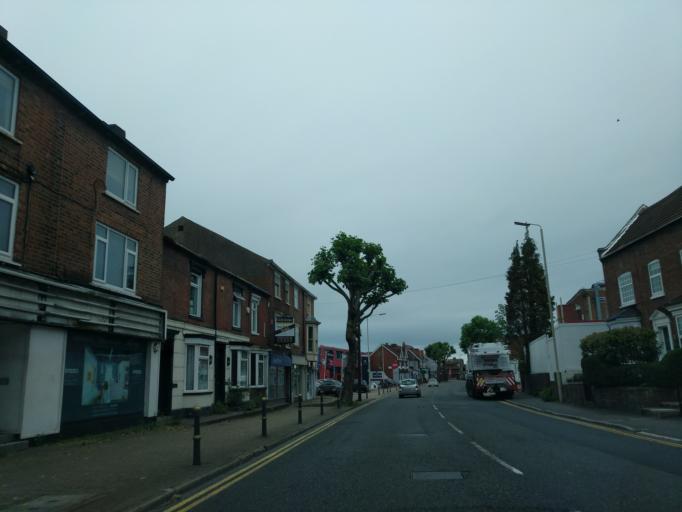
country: GB
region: England
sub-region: Dudley
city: Stourbridge
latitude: 52.4523
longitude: -2.1429
